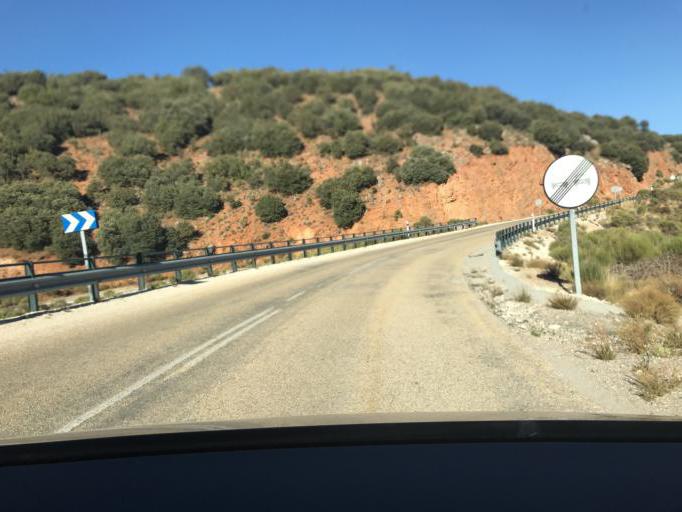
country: ES
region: Andalusia
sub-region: Provincia de Granada
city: Beas de Granada
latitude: 37.3003
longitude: -3.4485
